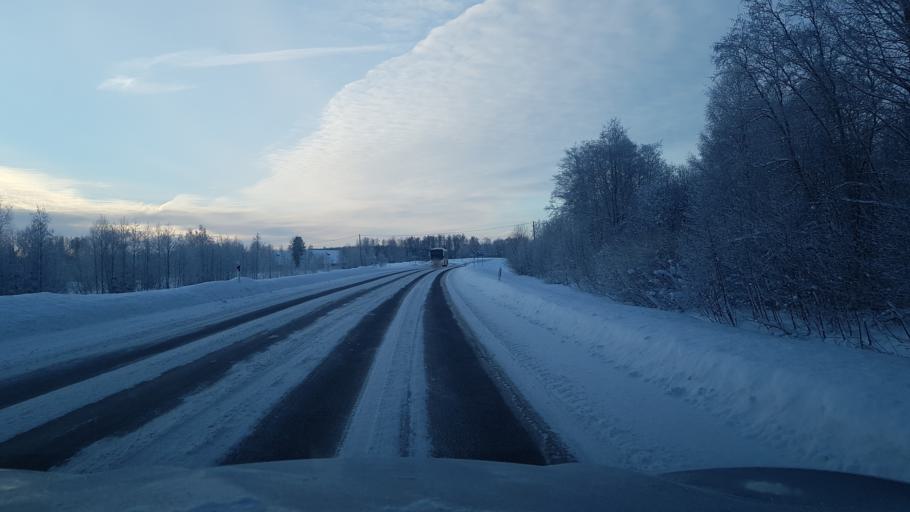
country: EE
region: Ida-Virumaa
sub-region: Johvi vald
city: Johvi
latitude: 59.3409
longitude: 27.4680
